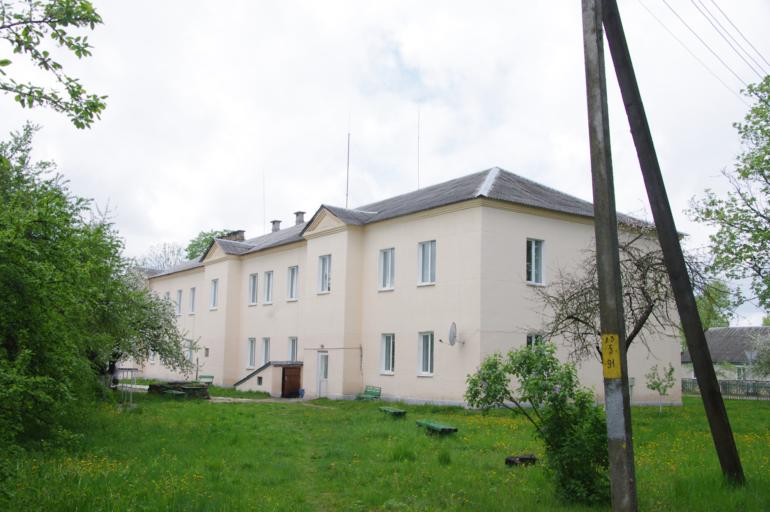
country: BY
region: Minsk
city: Narach
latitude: 54.9367
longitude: 26.6855
